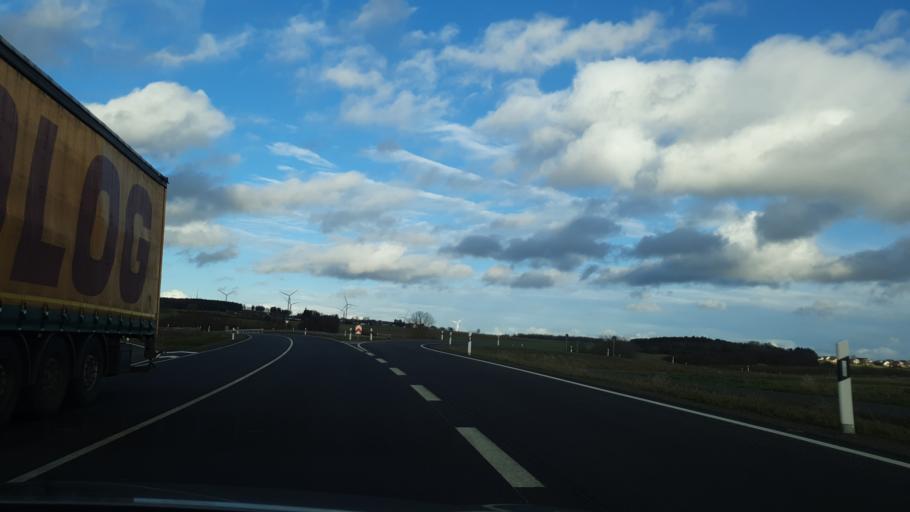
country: DE
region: Rheinland-Pfalz
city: Godenroth
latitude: 50.0837
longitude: 7.4975
